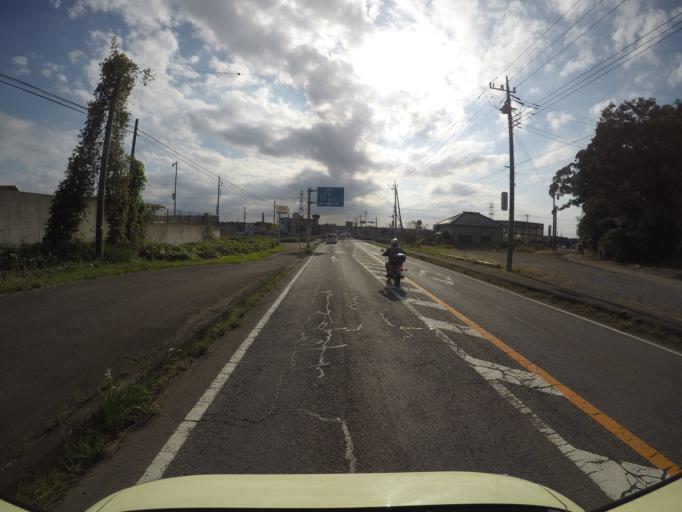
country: JP
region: Ibaraki
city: Iwai
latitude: 35.9930
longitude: 139.9016
